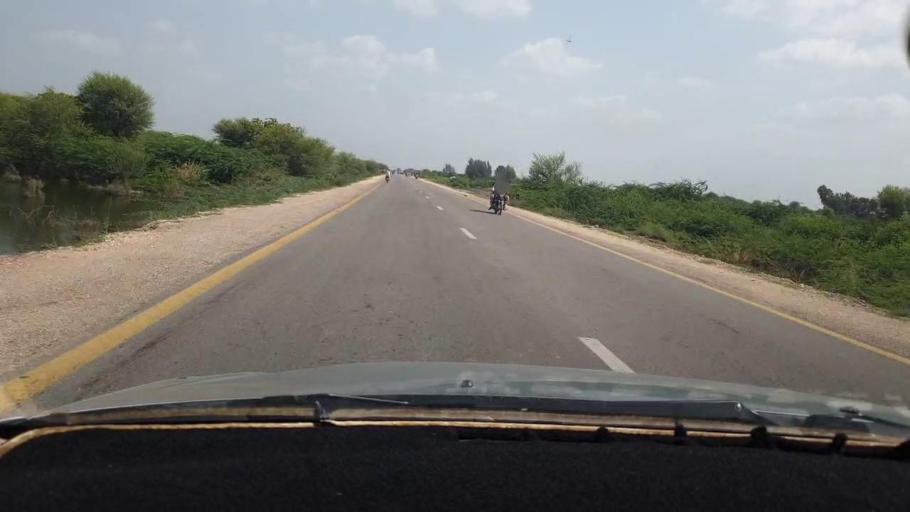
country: PK
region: Sindh
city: Digri
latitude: 25.1122
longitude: 69.1598
